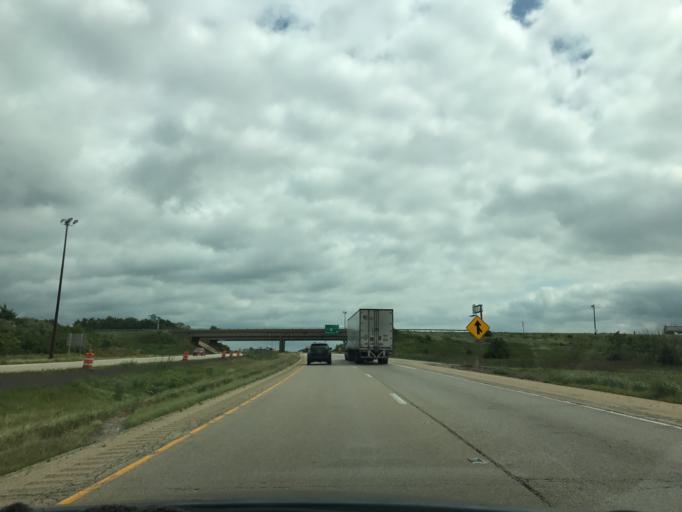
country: US
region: Illinois
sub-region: LaSalle County
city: La Salle
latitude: 41.3678
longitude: -89.0624
